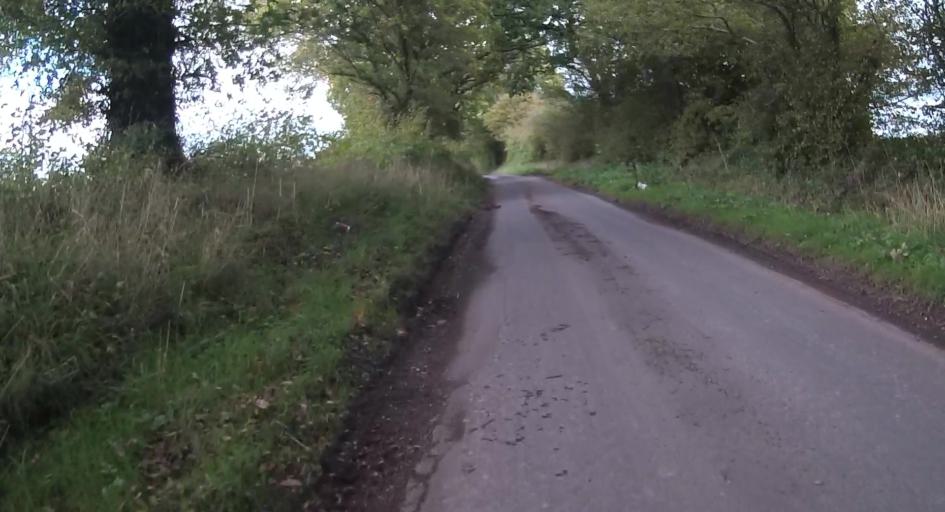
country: GB
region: England
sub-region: Hampshire
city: Alton
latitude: 51.1616
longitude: -0.9261
